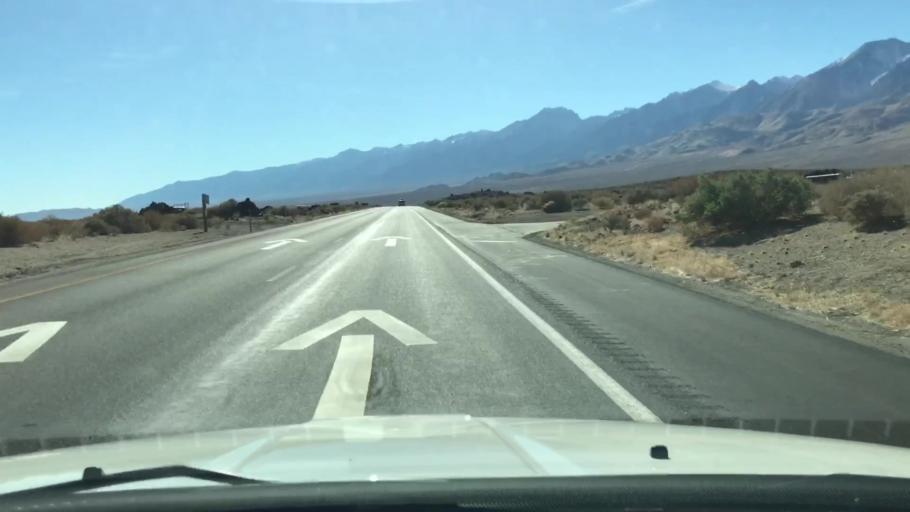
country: US
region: California
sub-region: Inyo County
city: Big Pine
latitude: 36.9323
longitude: -118.2411
